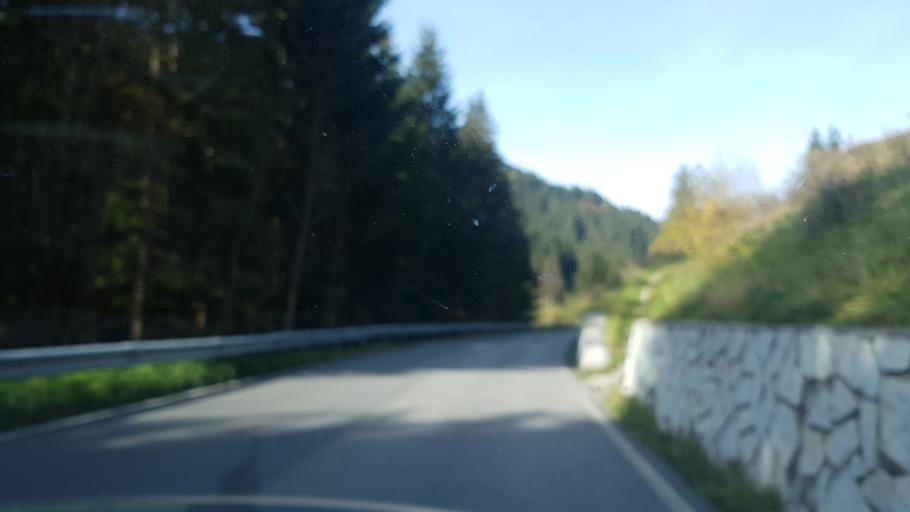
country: IT
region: Veneto
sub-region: Provincia di Belluno
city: Santo Stefano di Cadore
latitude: 46.5675
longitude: 12.5403
